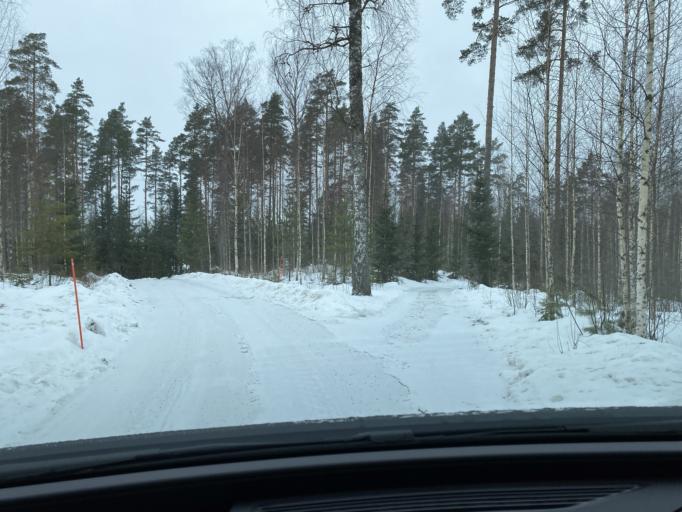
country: FI
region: Haeme
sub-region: Forssa
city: Humppila
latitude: 61.0566
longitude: 23.2591
